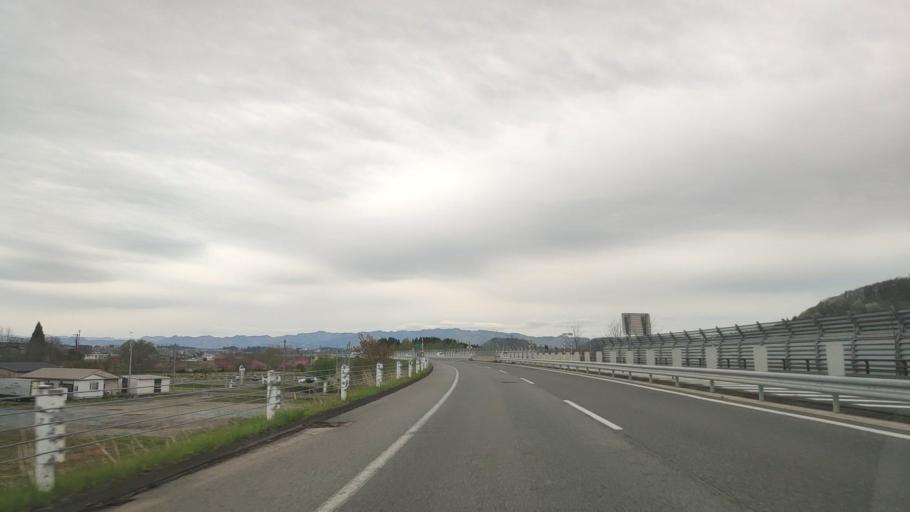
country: JP
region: Akita
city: Odate
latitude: 40.3009
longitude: 140.5573
